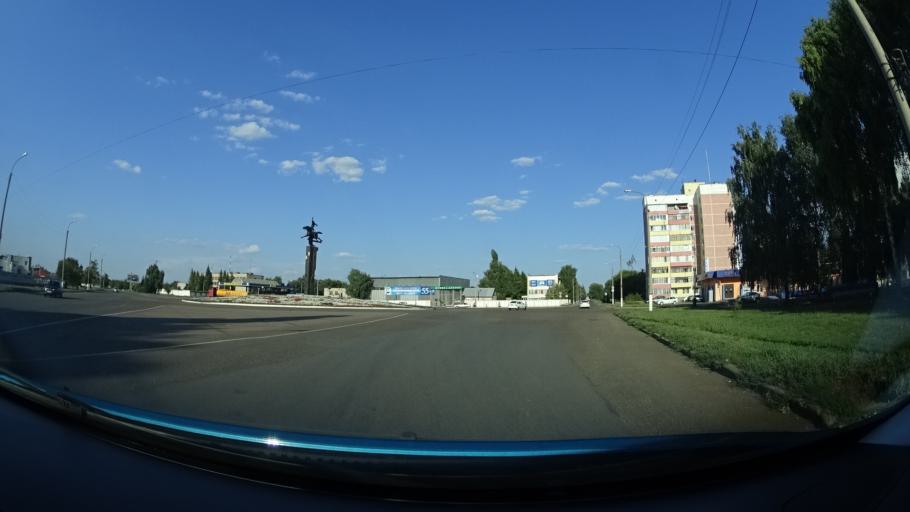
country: RU
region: Bashkortostan
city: Salavat
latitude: 53.3730
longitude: 55.9243
